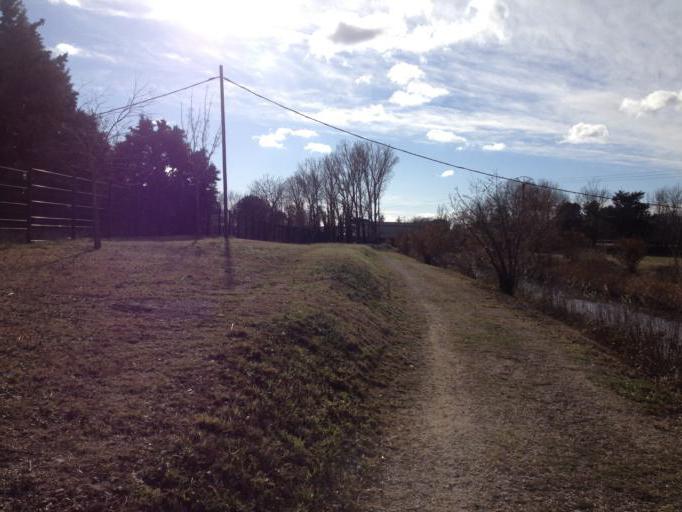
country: FR
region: Provence-Alpes-Cote d'Azur
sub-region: Departement du Vaucluse
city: Orange
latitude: 44.1298
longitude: 4.7942
